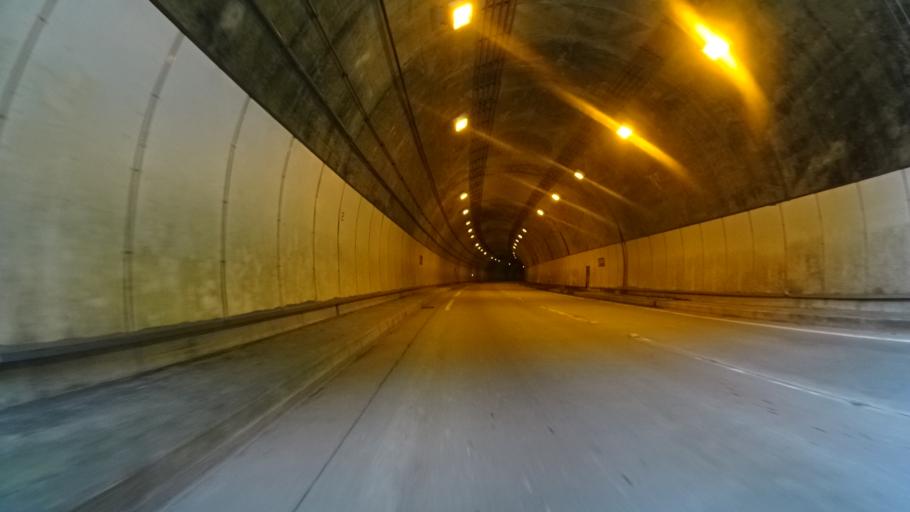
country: JP
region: Yamanashi
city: Uenohara
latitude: 35.6962
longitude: 139.1035
